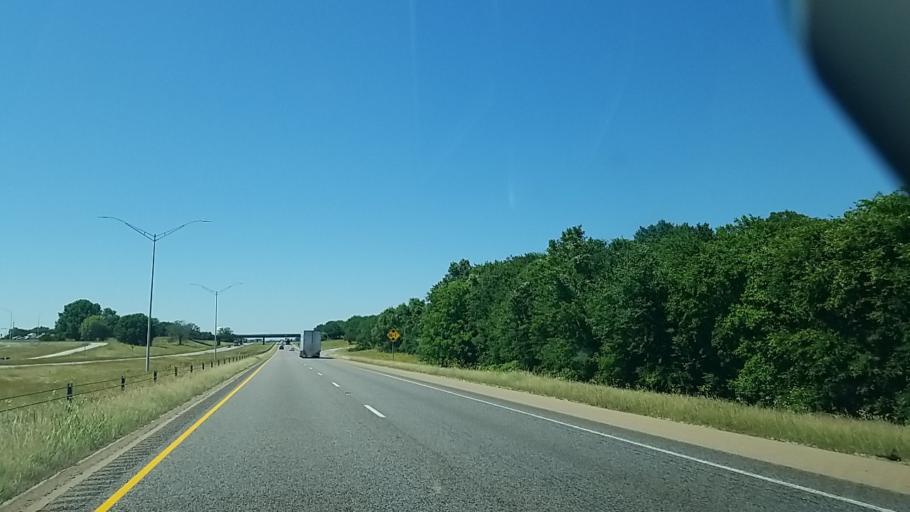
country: US
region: Texas
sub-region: Freestone County
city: Fairfield
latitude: 31.7101
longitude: -96.1750
